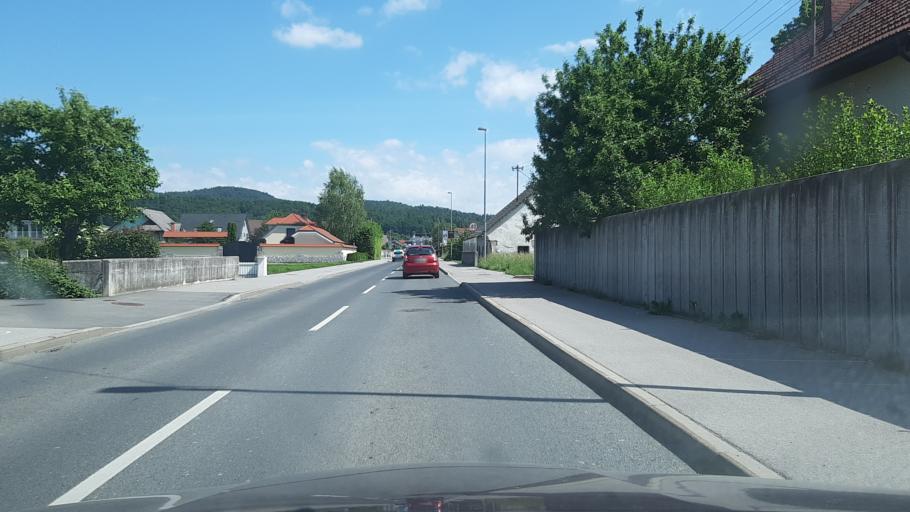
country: SI
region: Brezovica
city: Vnanje Gorice
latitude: 46.0152
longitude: 14.4141
